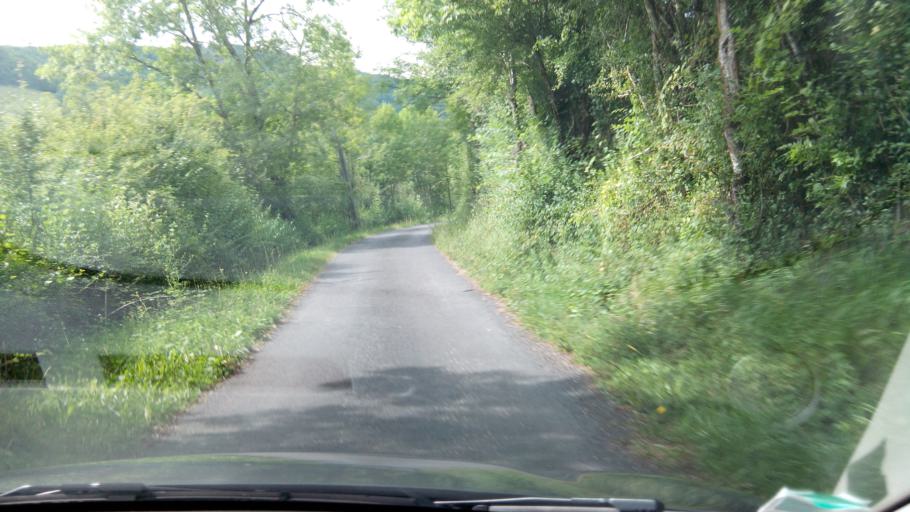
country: FR
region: Limousin
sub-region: Departement de la Correze
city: Cosnac
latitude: 45.0571
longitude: 1.5791
